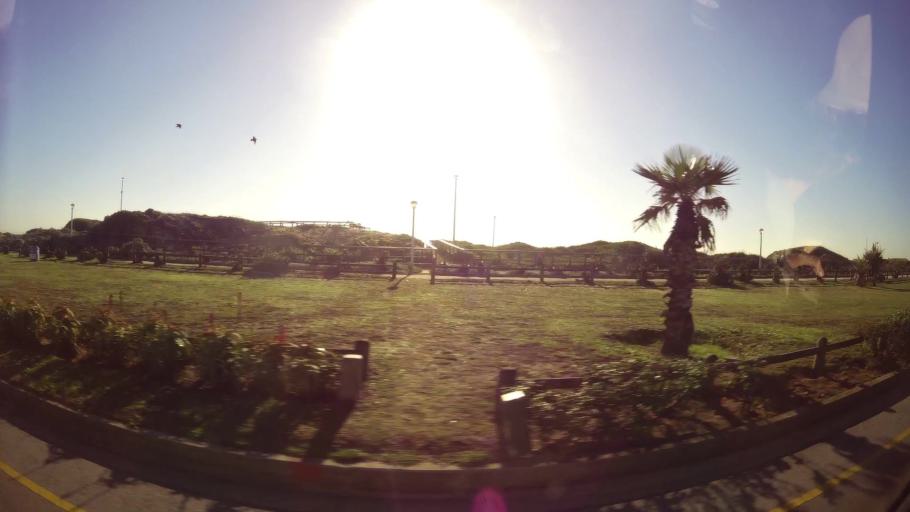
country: ZA
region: Eastern Cape
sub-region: Nelson Mandela Bay Metropolitan Municipality
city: Port Elizabeth
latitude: -33.9900
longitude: 25.6741
